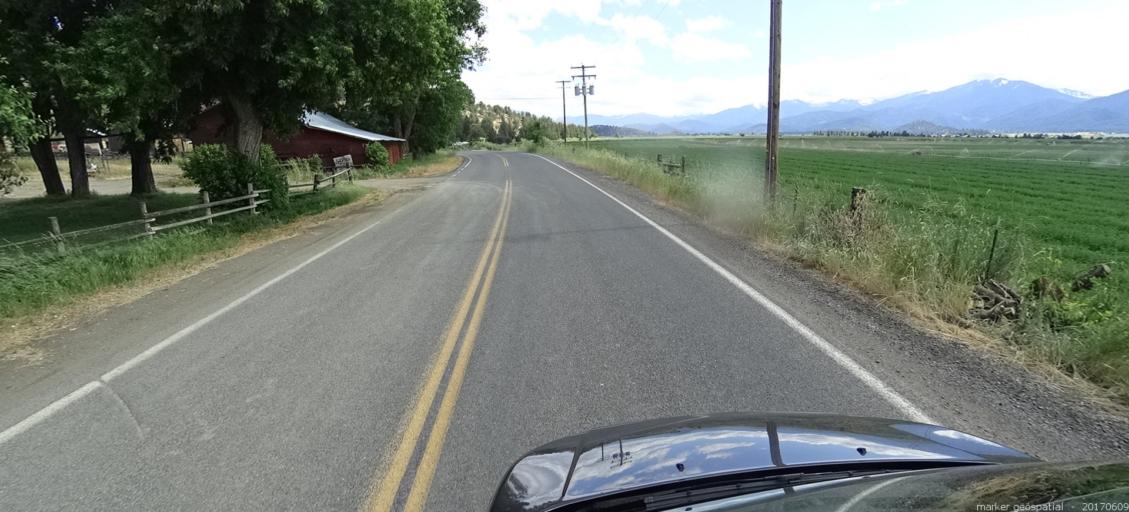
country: US
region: California
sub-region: Siskiyou County
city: Yreka
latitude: 41.5188
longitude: -122.8411
